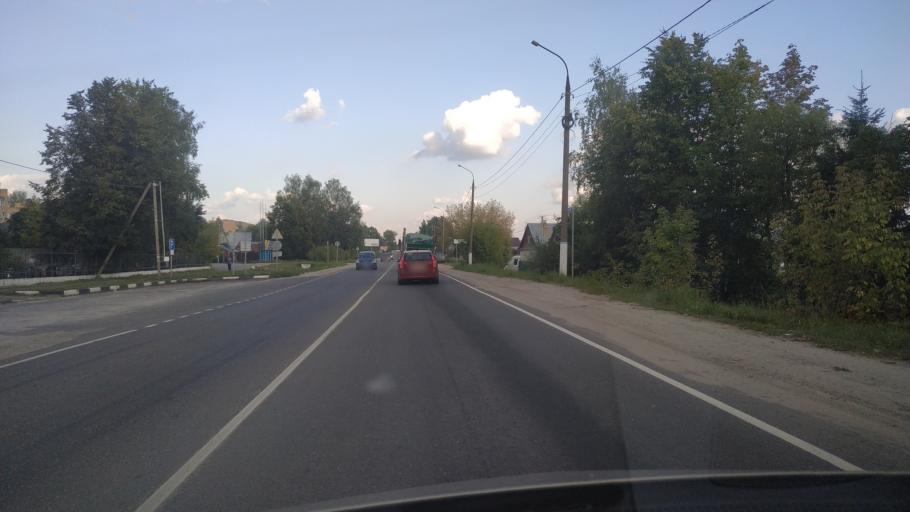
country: RU
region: Moskovskaya
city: Shatura
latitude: 55.5778
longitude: 39.4883
